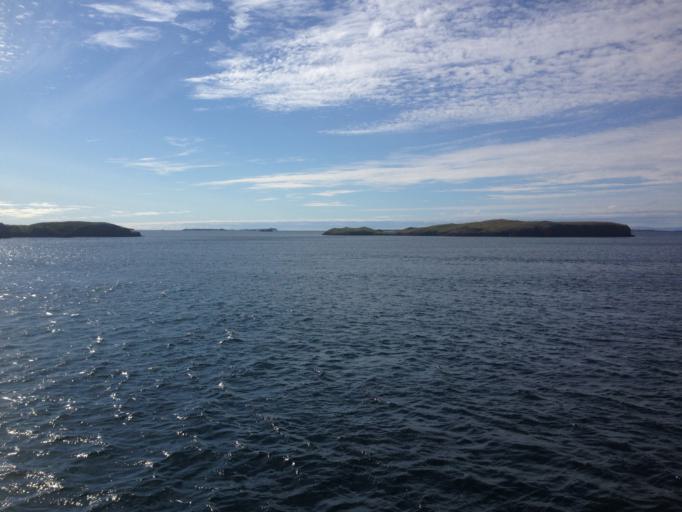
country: IS
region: West
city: Stykkisholmur
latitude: 65.1271
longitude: -22.5918
